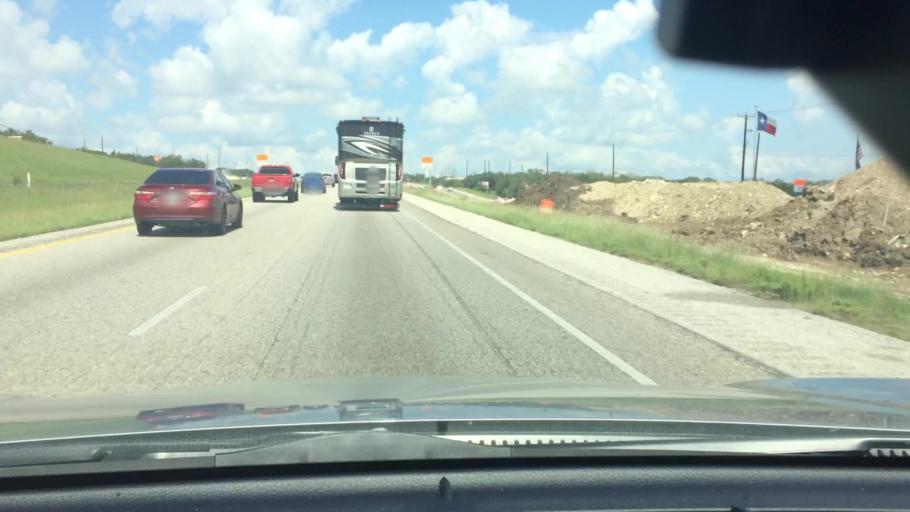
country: US
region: Texas
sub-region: Bexar County
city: Scenic Oaks
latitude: 29.7129
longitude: -98.6598
